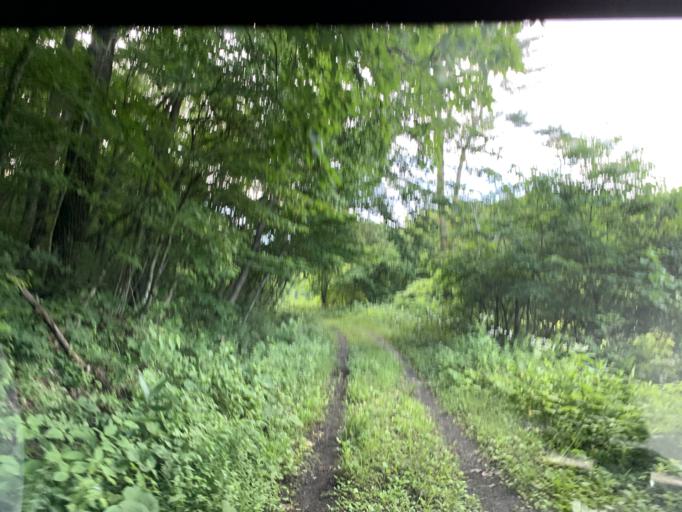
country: JP
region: Iwate
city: Ichinoseki
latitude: 38.9070
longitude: 140.9501
